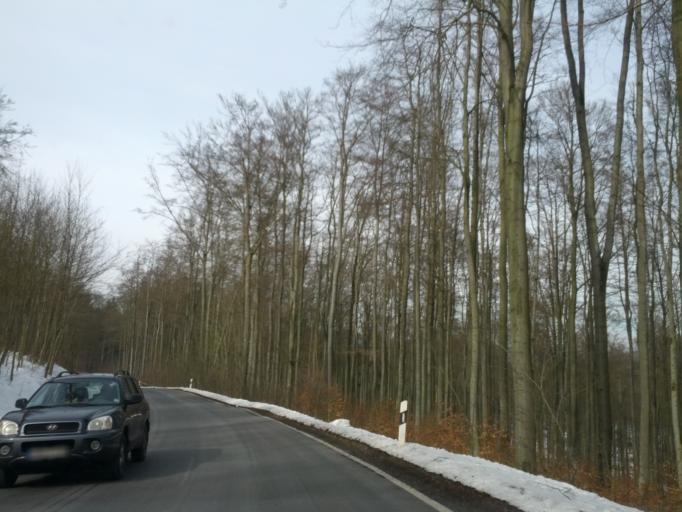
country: DE
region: Thuringia
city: Ruhla
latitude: 50.8679
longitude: 10.3818
